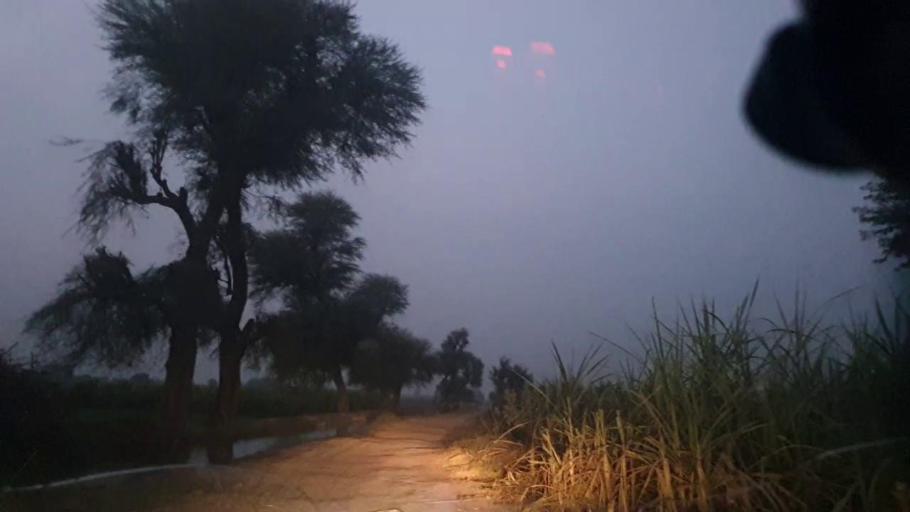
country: PK
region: Sindh
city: Hingorja
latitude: 27.2065
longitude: 68.3715
